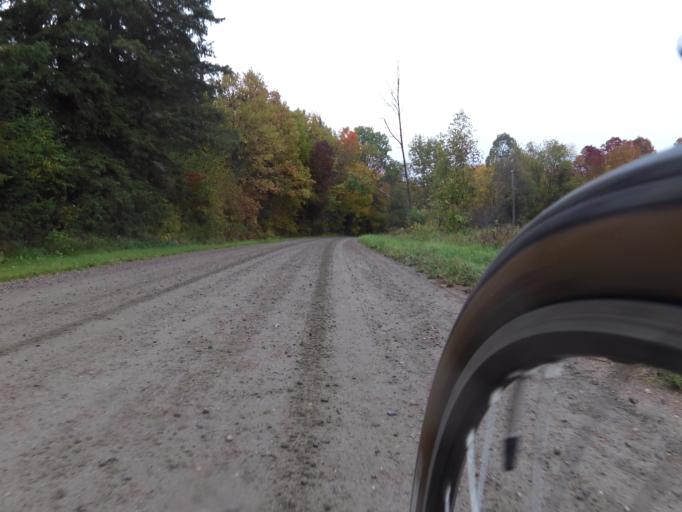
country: CA
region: Quebec
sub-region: Outaouais
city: Shawville
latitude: 45.6881
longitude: -76.5651
